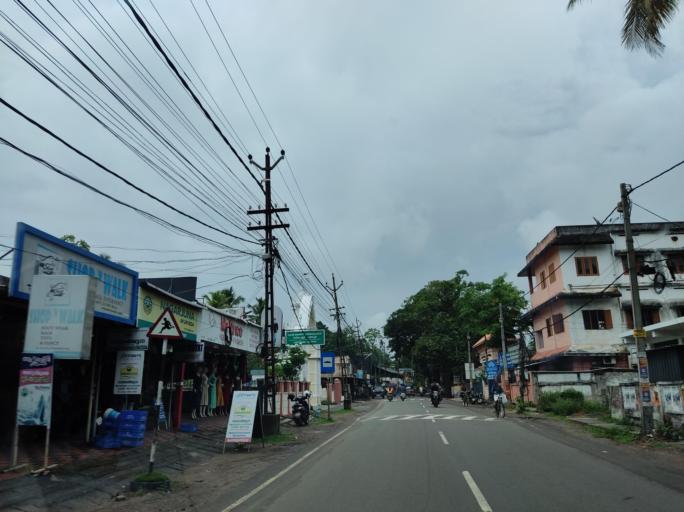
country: IN
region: Kerala
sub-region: Alappuzha
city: Mavelikara
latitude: 9.2438
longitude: 76.5199
